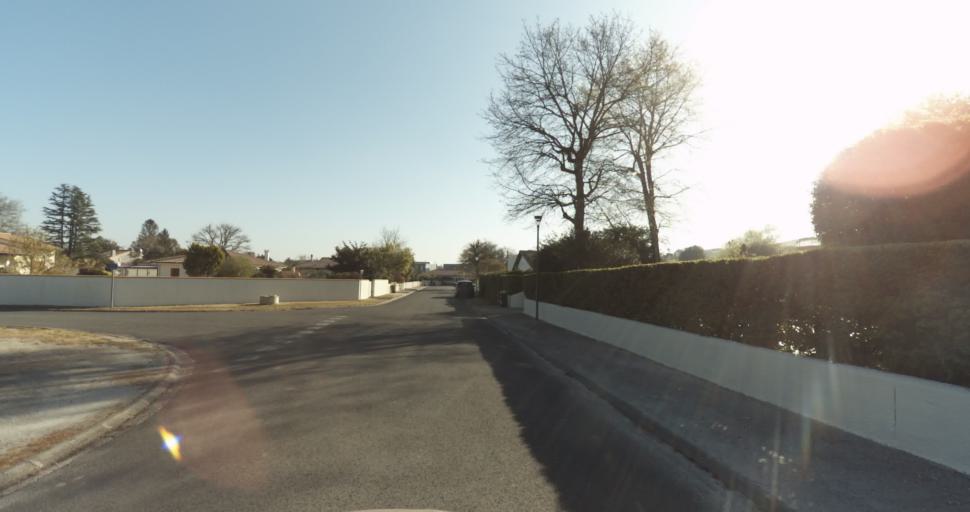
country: FR
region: Aquitaine
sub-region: Departement de la Gironde
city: Martignas-sur-Jalle
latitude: 44.8100
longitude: -0.7860
